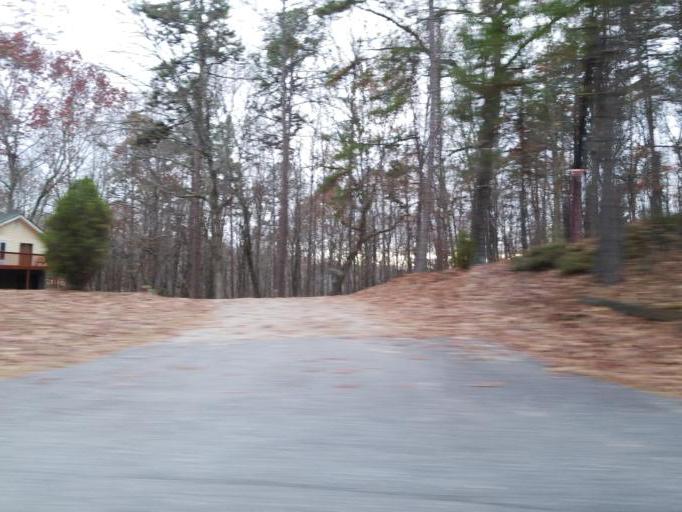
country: US
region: Georgia
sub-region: Dawson County
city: Dawsonville
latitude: 34.4250
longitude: -84.0509
